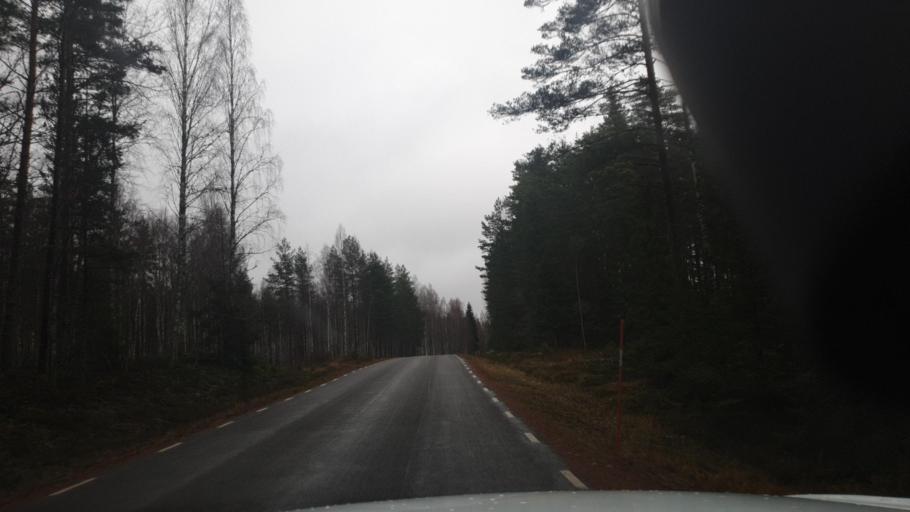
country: SE
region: Vaermland
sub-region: Arvika Kommun
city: Arvika
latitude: 59.5296
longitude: 12.3888
